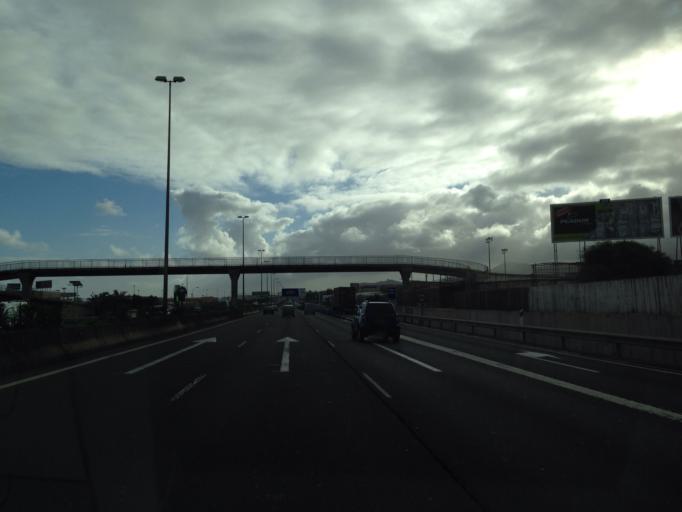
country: ES
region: Canary Islands
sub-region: Provincia de Las Palmas
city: Telde
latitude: 28.0163
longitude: -15.3875
